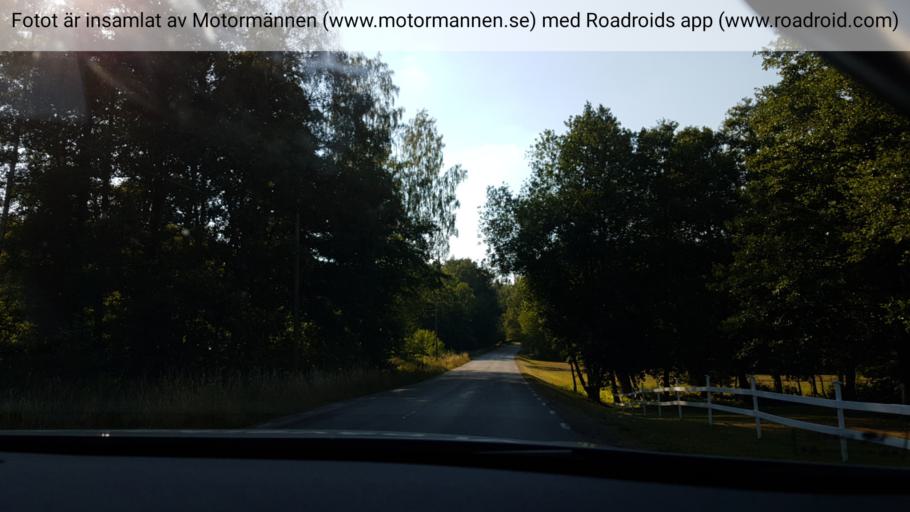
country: SE
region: Vaestra Goetaland
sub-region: Skovde Kommun
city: Stopen
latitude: 58.4985
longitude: 13.8216
